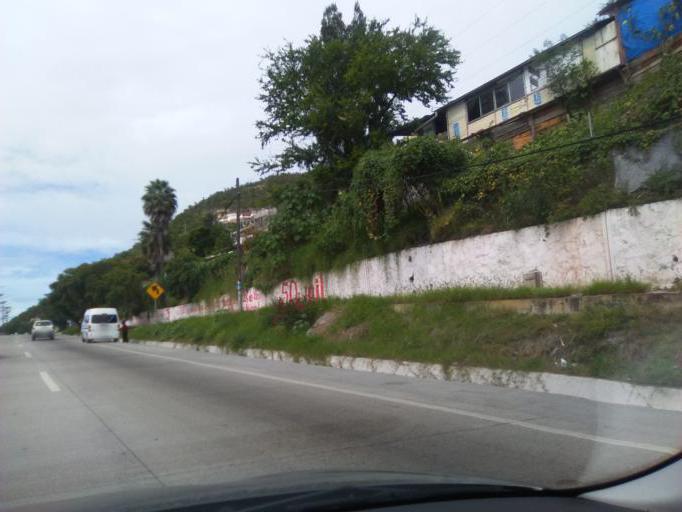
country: MX
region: Guerrero
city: Chilpancingo de los Bravos
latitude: 17.5912
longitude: -99.5175
